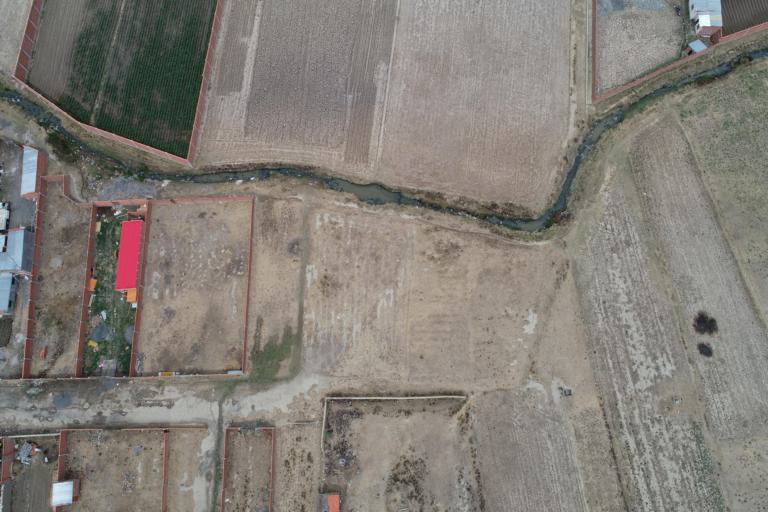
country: BO
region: La Paz
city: Achacachi
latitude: -16.0535
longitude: -68.6843
